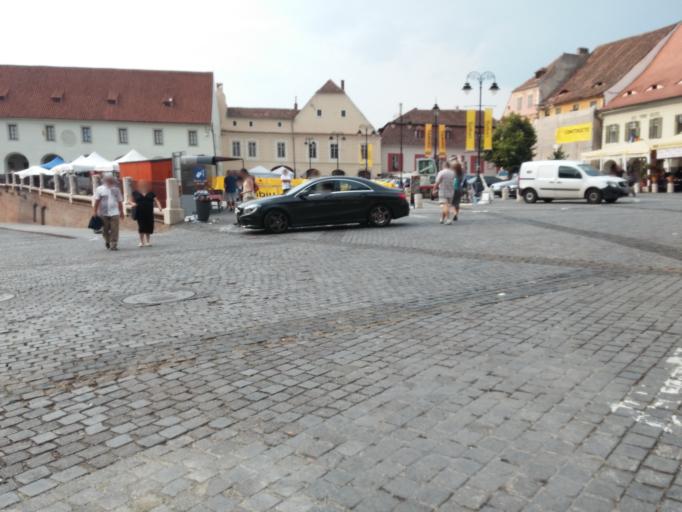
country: RO
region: Sibiu
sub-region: Municipiul Sibiu
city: Sibiu
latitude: 45.7978
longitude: 24.1518
